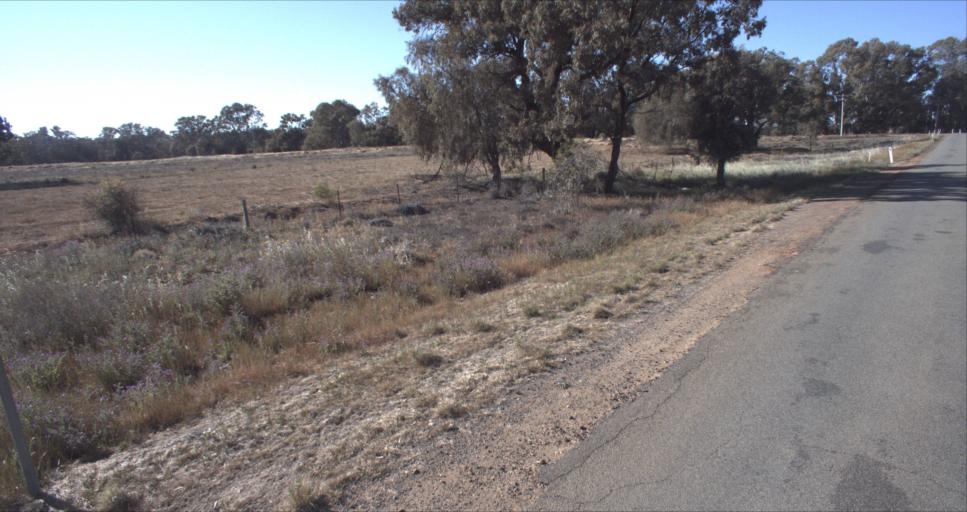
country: AU
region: New South Wales
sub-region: Leeton
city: Leeton
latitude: -34.6039
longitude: 146.2571
